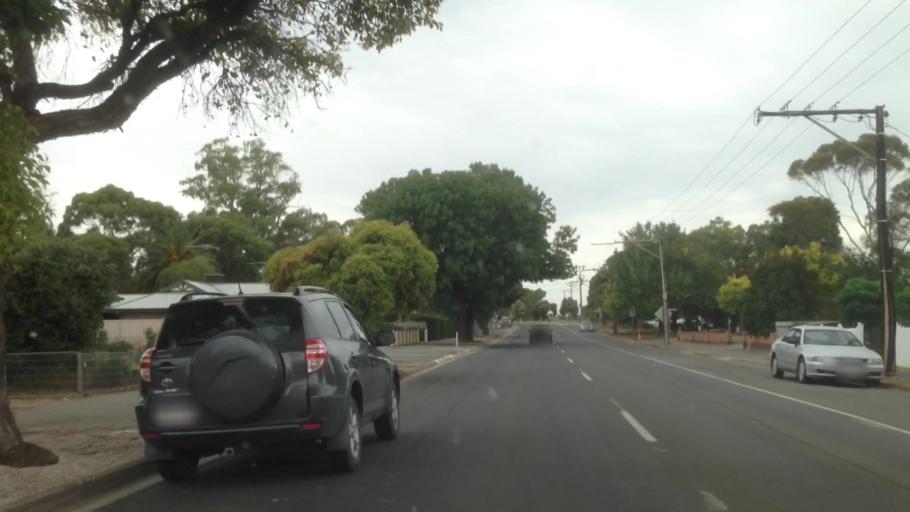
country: AU
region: South Australia
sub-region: Barossa
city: Lyndoch
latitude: -34.6029
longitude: 138.8912
